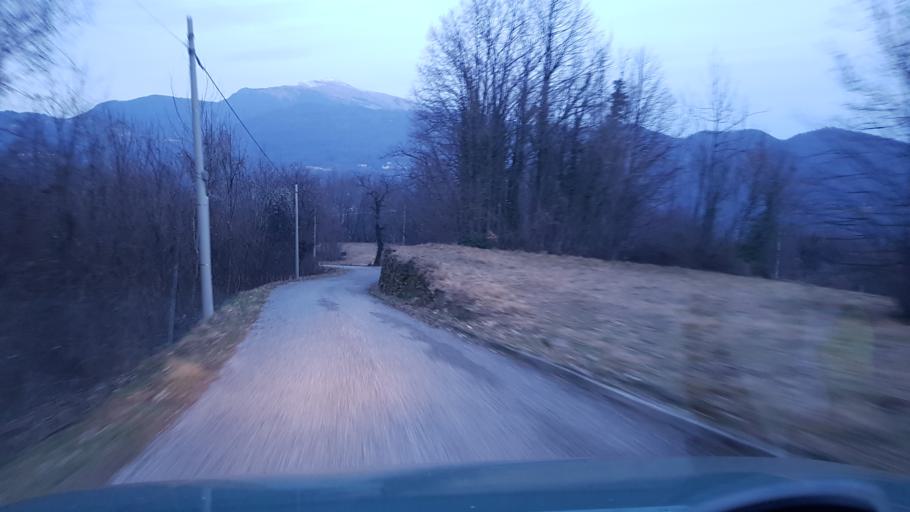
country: IT
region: Friuli Venezia Giulia
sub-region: Provincia di Udine
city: Pulfero
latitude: 46.1530
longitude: 13.4706
